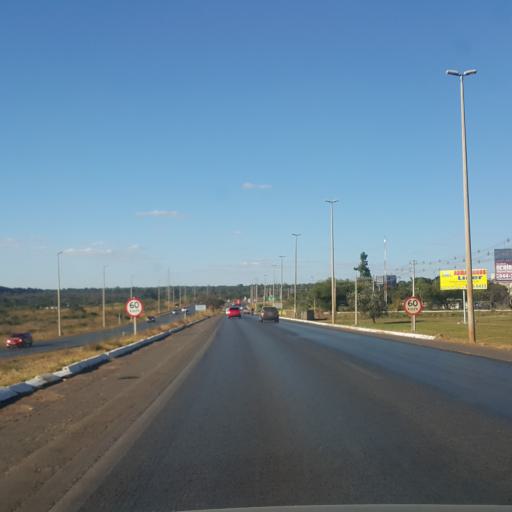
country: BR
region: Federal District
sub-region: Brasilia
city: Brasilia
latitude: -15.8014
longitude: -48.0781
